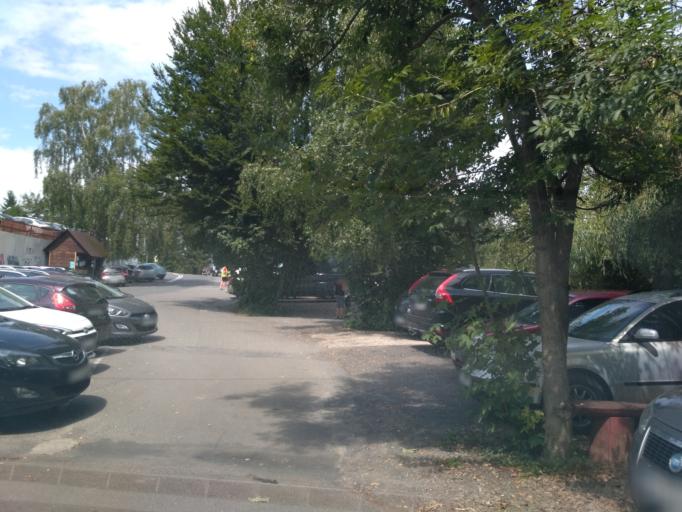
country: PL
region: Subcarpathian Voivodeship
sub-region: Powiat leski
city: Polanczyk
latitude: 49.3984
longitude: 22.4504
